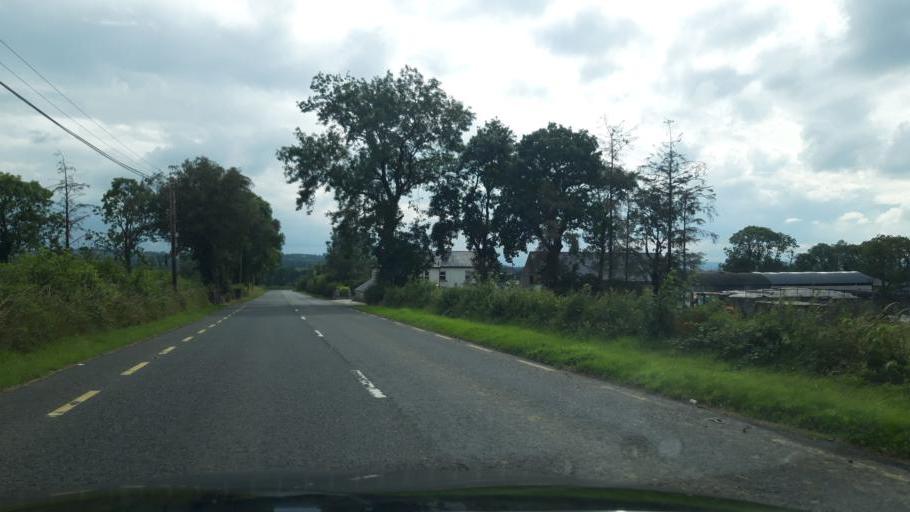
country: IE
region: Leinster
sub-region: Kilkenny
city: Castlecomer
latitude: 52.8519
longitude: -7.1208
